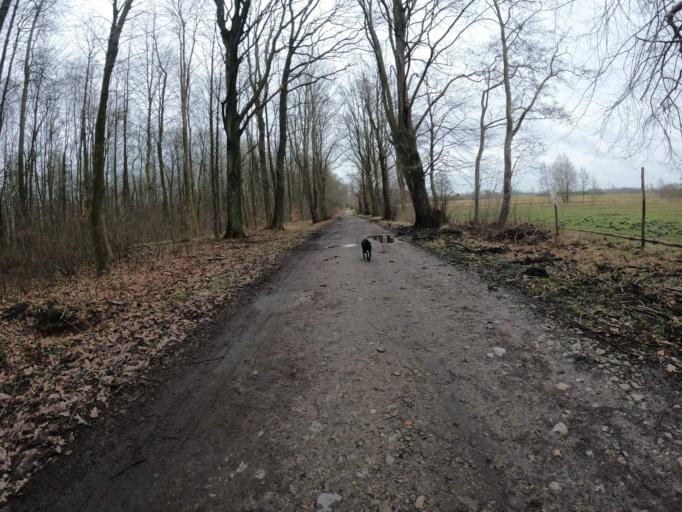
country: PL
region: West Pomeranian Voivodeship
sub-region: Powiat slawienski
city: Darlowo
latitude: 54.4044
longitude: 16.4439
